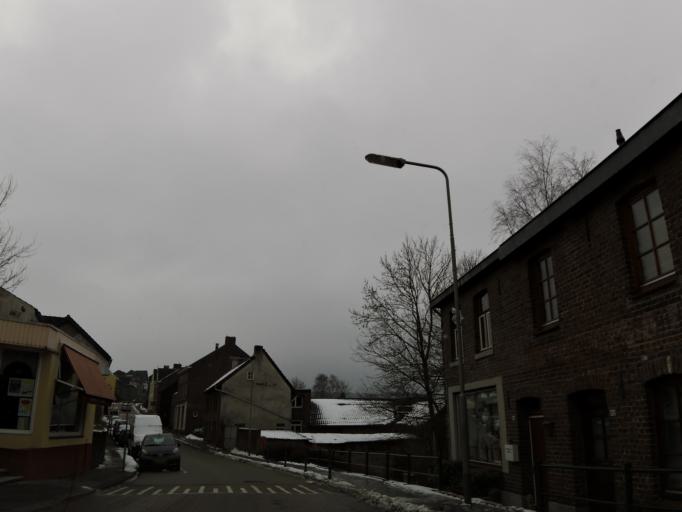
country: NL
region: Limburg
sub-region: Gemeente Simpelveld
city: Simpelveld
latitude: 50.7871
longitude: 5.9633
